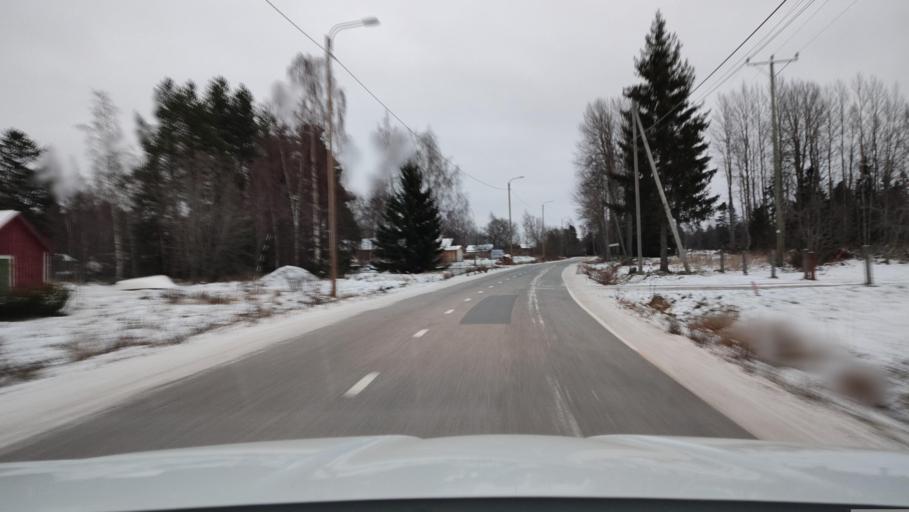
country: FI
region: Ostrobothnia
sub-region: Vaasa
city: Replot
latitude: 63.3492
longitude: 21.3029
